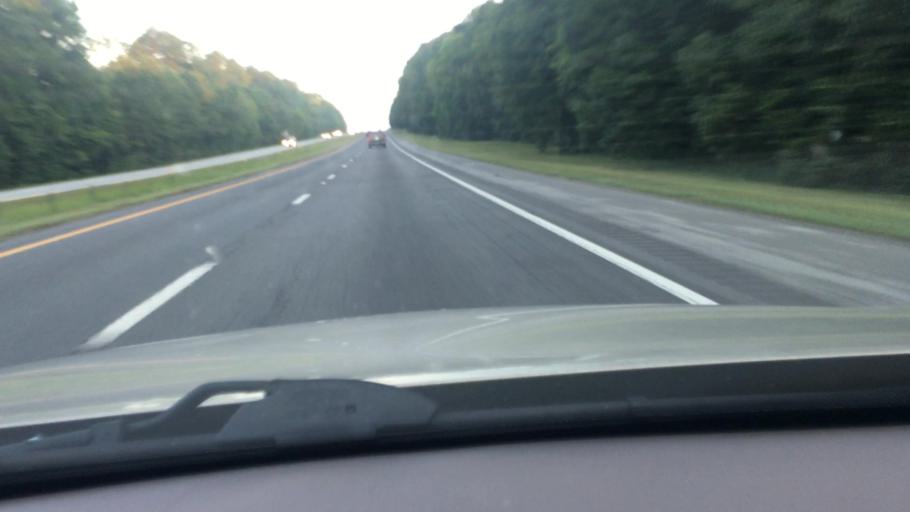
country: US
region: South Carolina
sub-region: Richland County
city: Lake Murray of Richland
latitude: 34.1533
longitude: -81.2558
